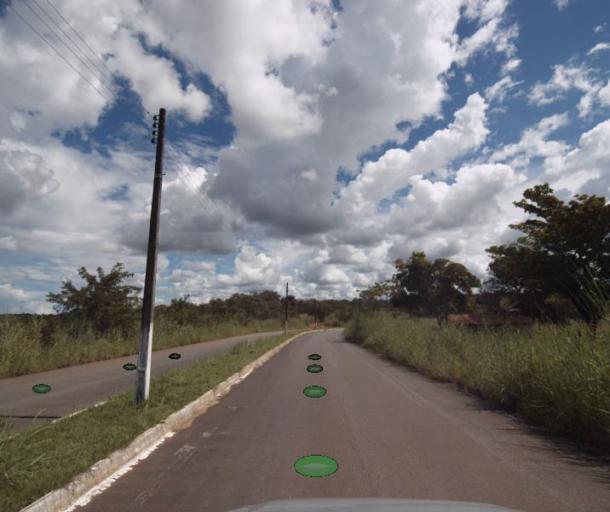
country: BR
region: Goias
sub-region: Porangatu
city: Porangatu
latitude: -13.7305
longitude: -49.0227
